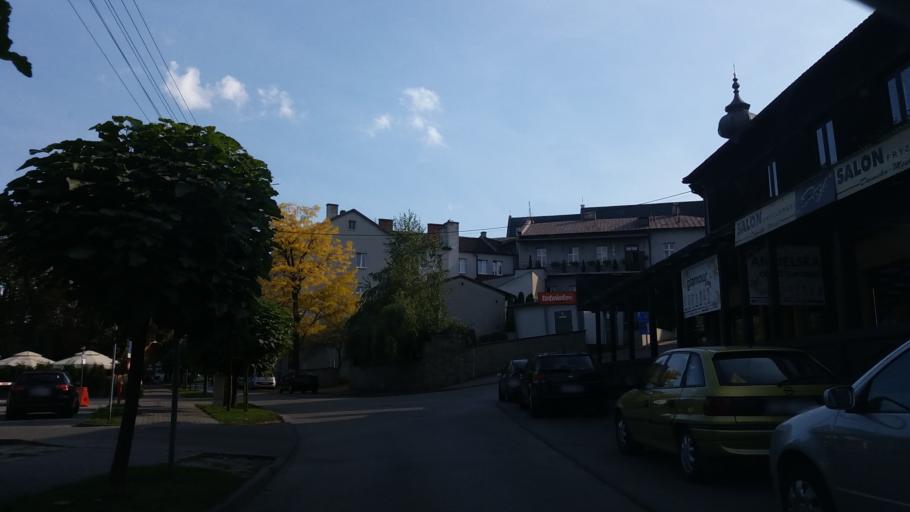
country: PL
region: Lesser Poland Voivodeship
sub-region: Powiat wadowicki
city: Wadowice
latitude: 49.8847
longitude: 19.4935
